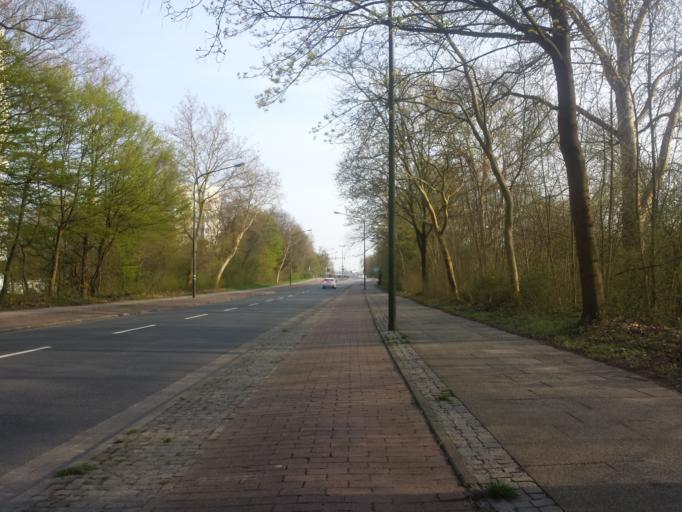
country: DE
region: Lower Saxony
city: Lilienthal
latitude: 53.0851
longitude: 8.8895
